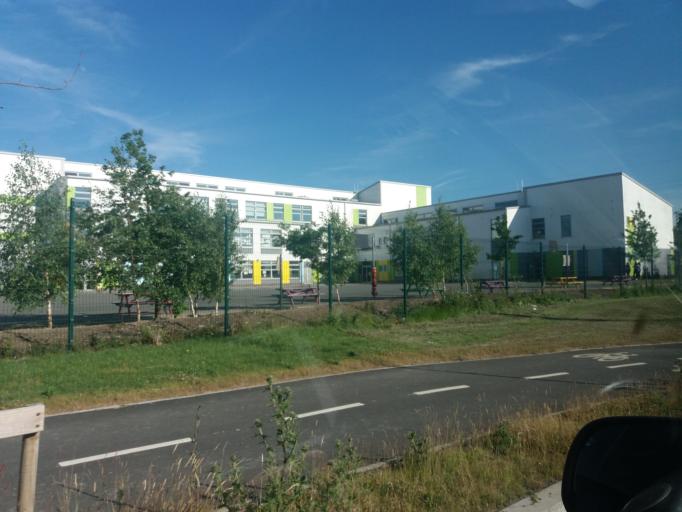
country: IE
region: Leinster
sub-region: Fingal County
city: Blanchardstown
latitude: 53.4242
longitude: -6.3829
